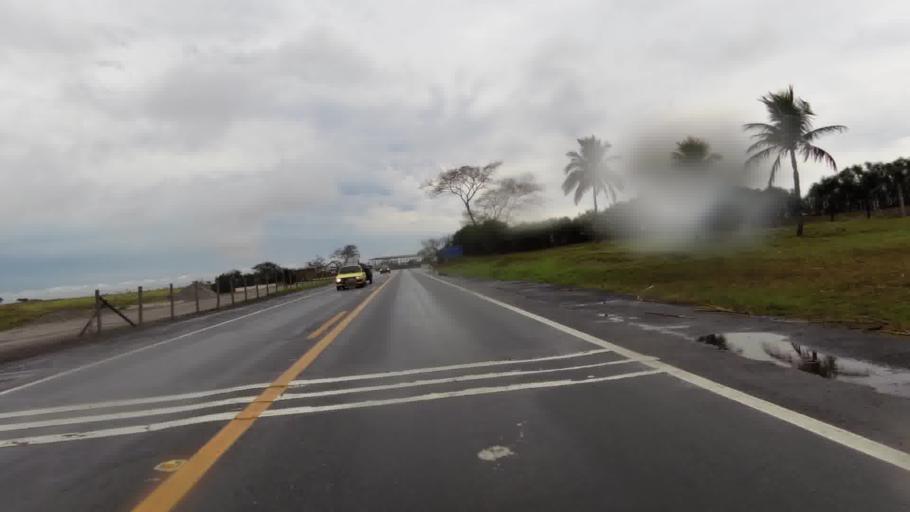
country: BR
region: Rio de Janeiro
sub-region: Campos Dos Goytacazes
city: Campos
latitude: -21.5343
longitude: -41.3411
